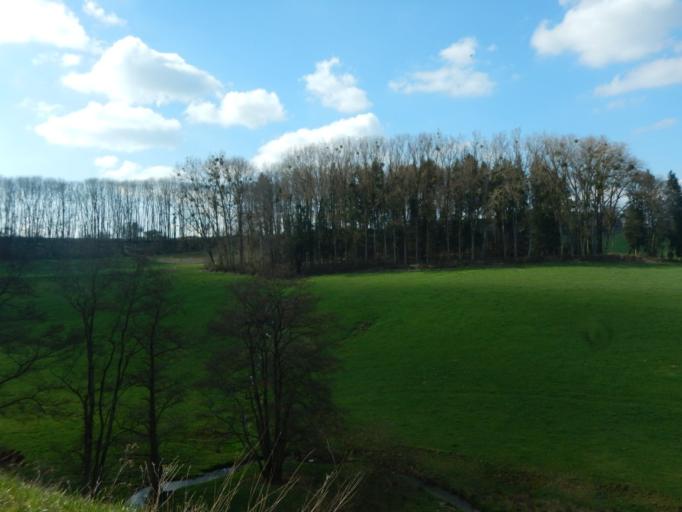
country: LU
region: Grevenmacher
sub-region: Canton d'Echternach
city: Beaufort
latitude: 49.8151
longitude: 6.2676
